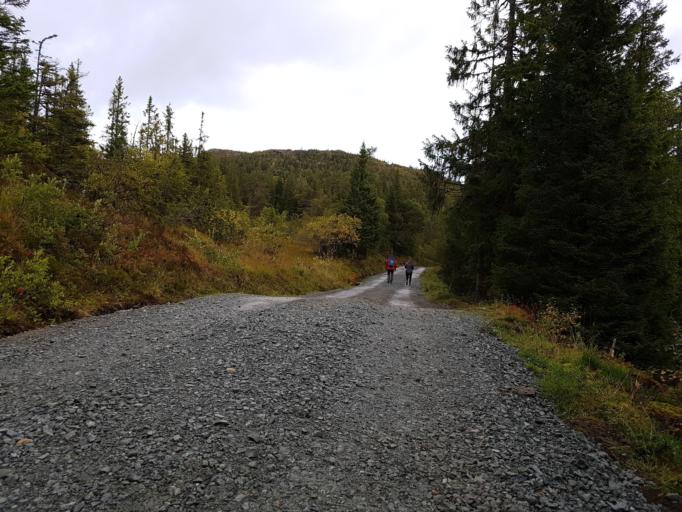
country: NO
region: Sor-Trondelag
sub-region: Melhus
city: Melhus
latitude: 63.4147
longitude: 10.2383
